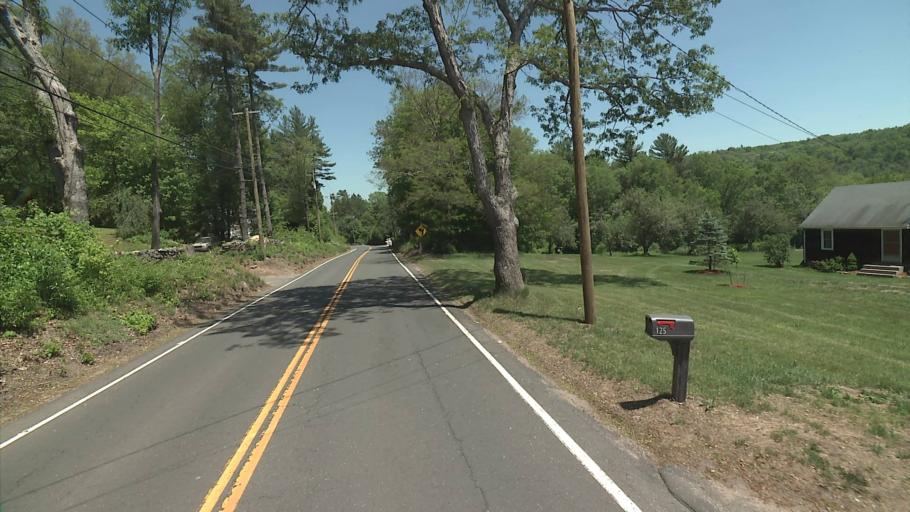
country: US
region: Connecticut
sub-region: Tolland County
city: Stafford
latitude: 41.9698
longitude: -72.2912
